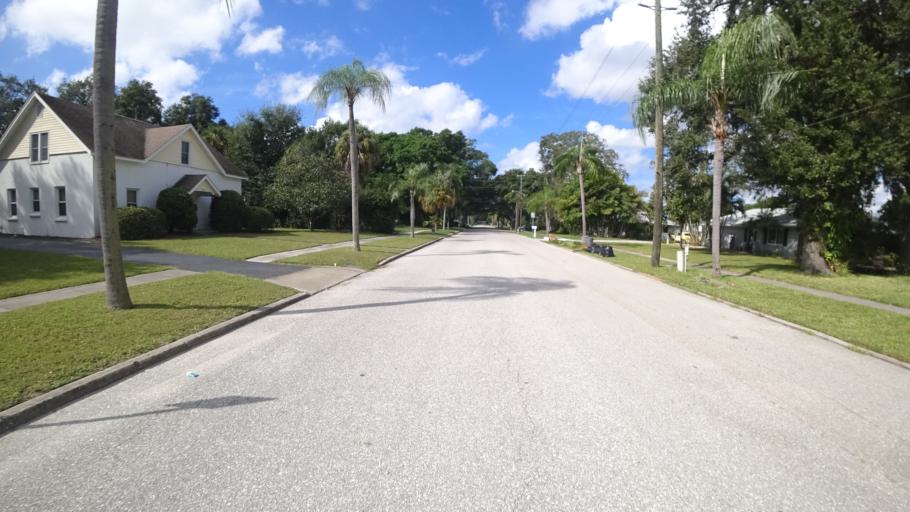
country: US
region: Florida
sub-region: Manatee County
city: Ellenton
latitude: 27.4988
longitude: -82.5390
